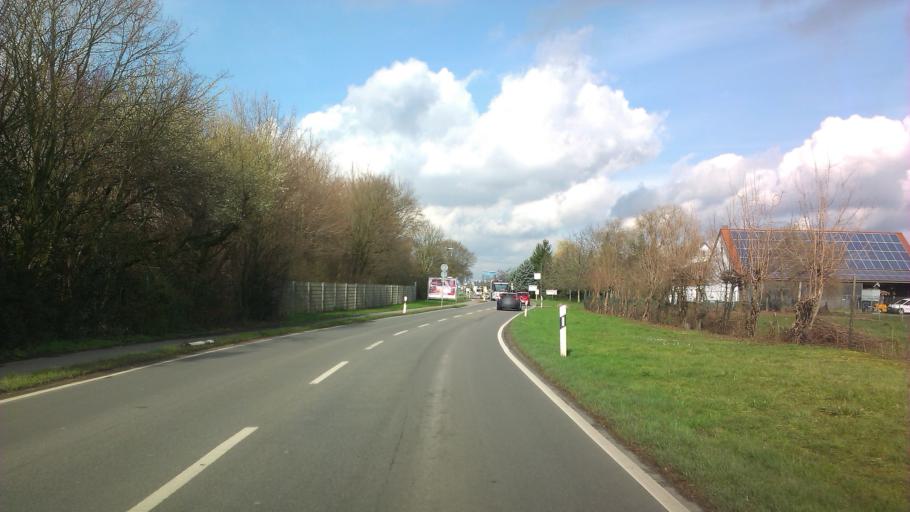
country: DE
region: Baden-Wuerttemberg
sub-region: Karlsruhe Region
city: Eppelheim
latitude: 49.3982
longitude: 8.6548
